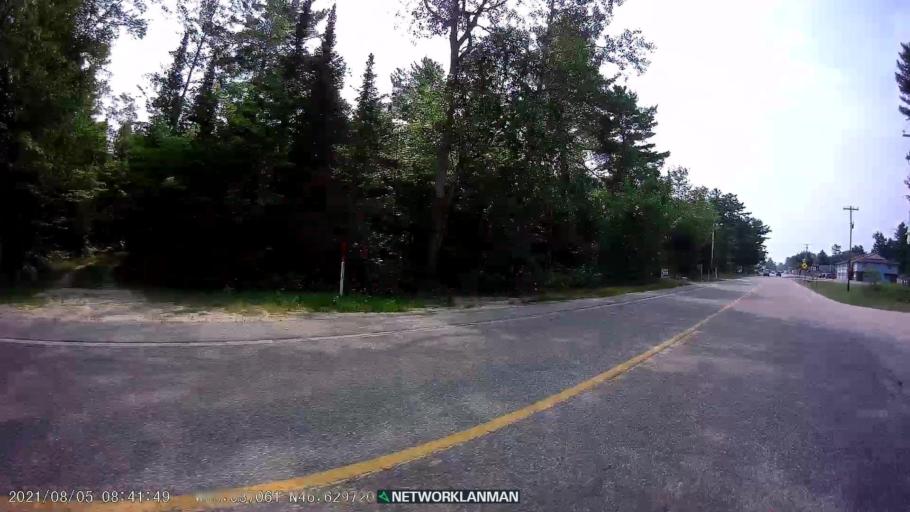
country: US
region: Michigan
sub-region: Luce County
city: Newberry
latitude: 46.6297
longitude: -85.0369
